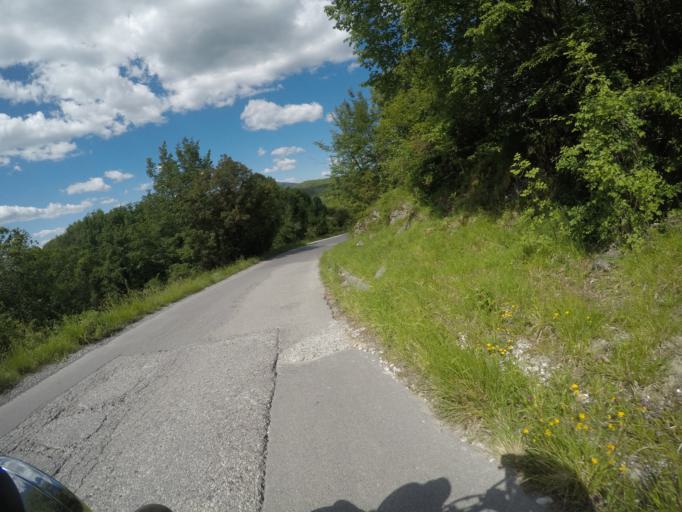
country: IT
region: Tuscany
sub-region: Provincia di Lucca
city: Minucciano
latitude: 44.1629
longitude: 10.2081
